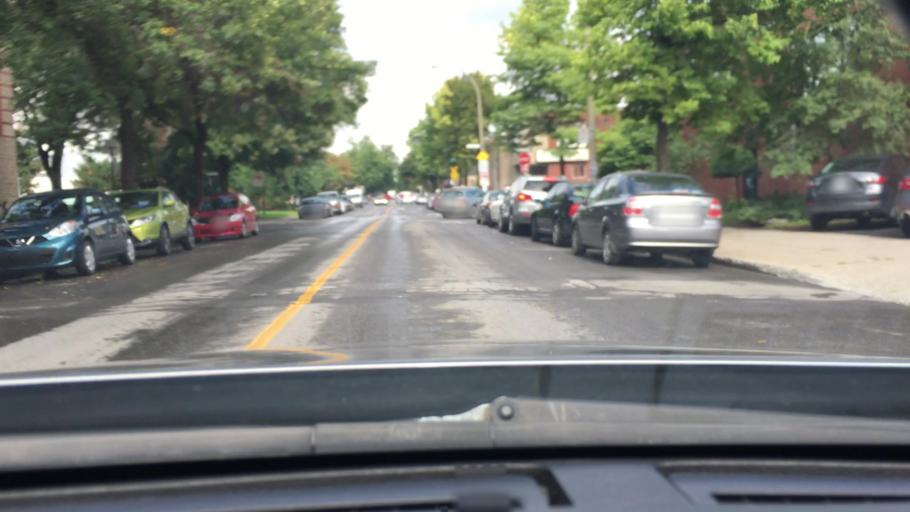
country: CA
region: Quebec
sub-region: Monteregie
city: Longueuil
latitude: 45.5402
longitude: -73.5519
